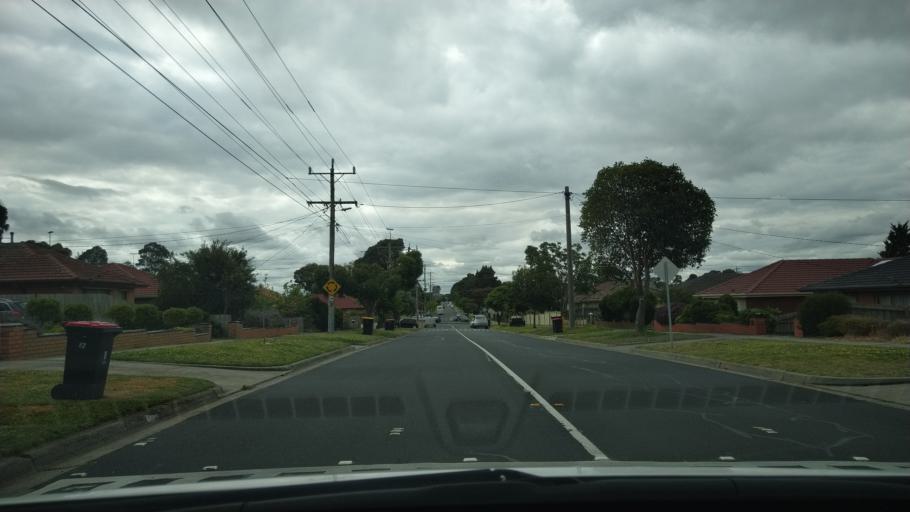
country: AU
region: Victoria
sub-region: Kingston
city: Mentone
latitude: -37.9611
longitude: 145.0719
